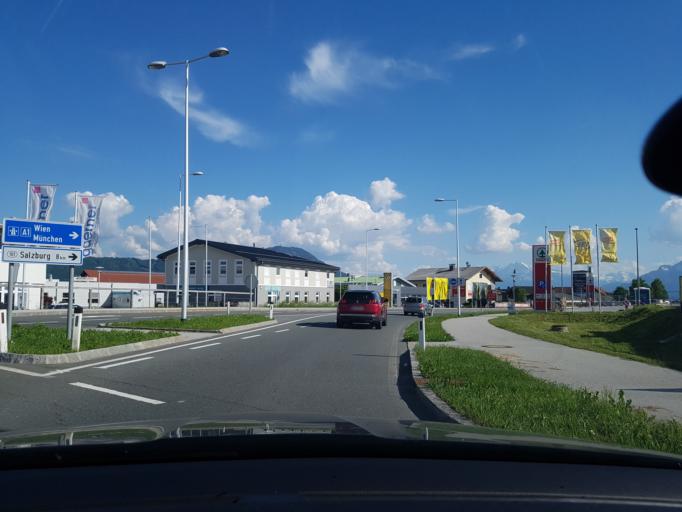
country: AT
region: Salzburg
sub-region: Politischer Bezirk Salzburg-Umgebung
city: Elixhausen
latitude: 47.8714
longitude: 13.0667
